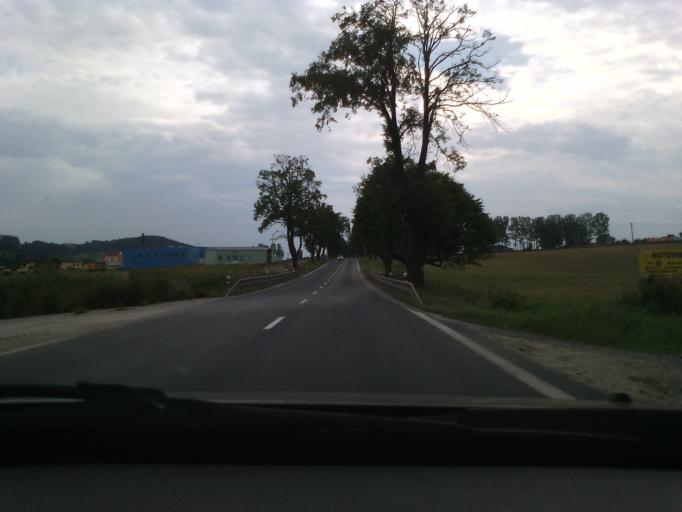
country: SK
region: Presovsky
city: Spisska Bela
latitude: 49.1678
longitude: 20.4480
